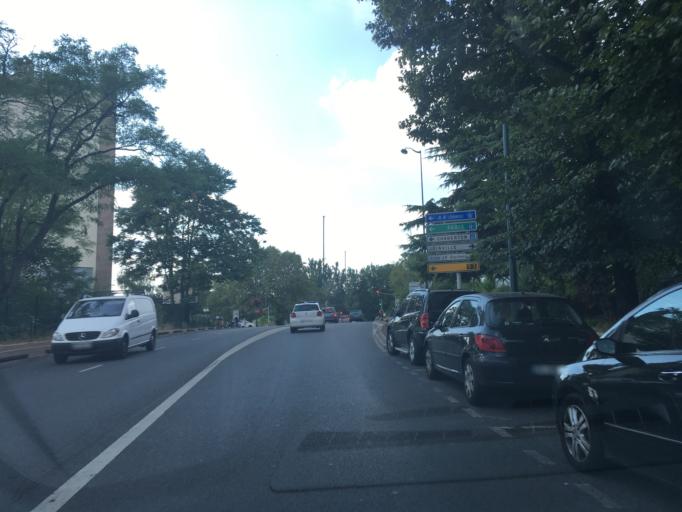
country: FR
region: Ile-de-France
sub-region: Departement du Val-de-Marne
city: Joinville-le-Pont
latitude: 48.8162
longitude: 2.4605
